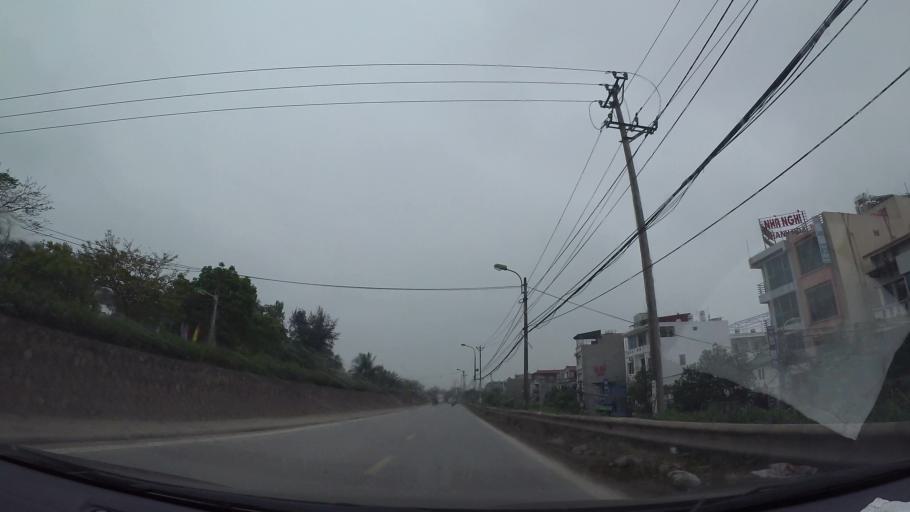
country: VN
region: Ha Noi
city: Hai BaTrung
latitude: 20.9979
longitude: 105.8892
